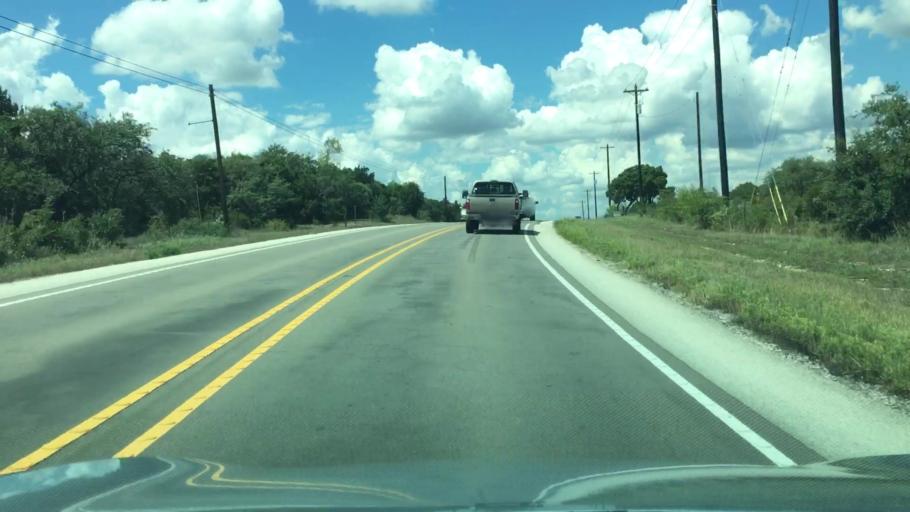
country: US
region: Texas
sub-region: Hays County
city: Woodcreek
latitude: 30.0790
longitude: -98.0974
